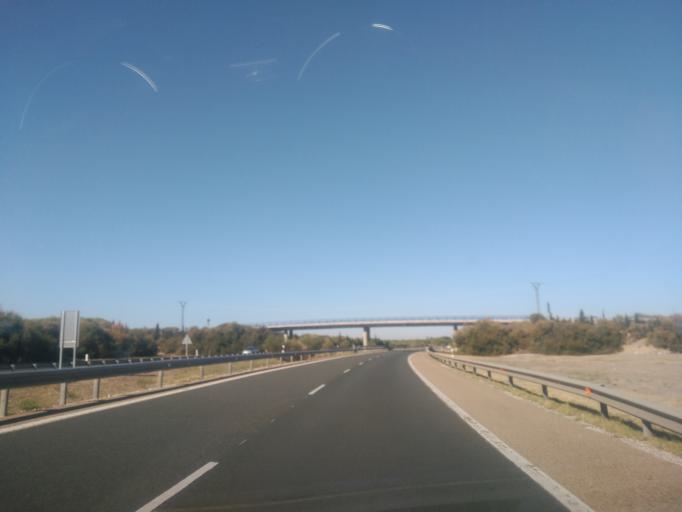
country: ES
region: Castille and Leon
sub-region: Provincia de Valladolid
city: Tudela de Duero
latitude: 41.5870
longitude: -4.5534
